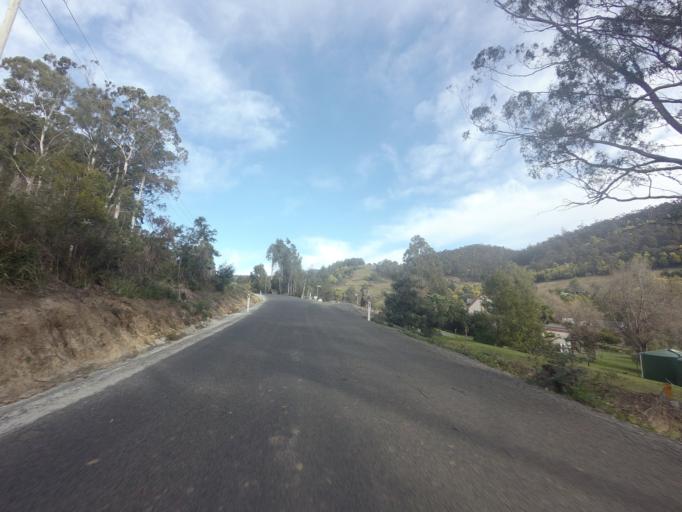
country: AU
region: Tasmania
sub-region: Kingborough
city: Margate
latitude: -42.9912
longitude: 147.1870
